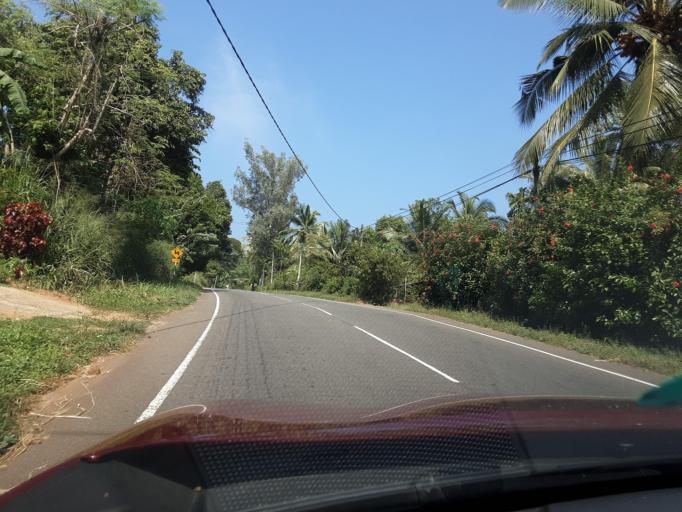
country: LK
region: Uva
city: Badulla
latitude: 7.1830
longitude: 81.0456
